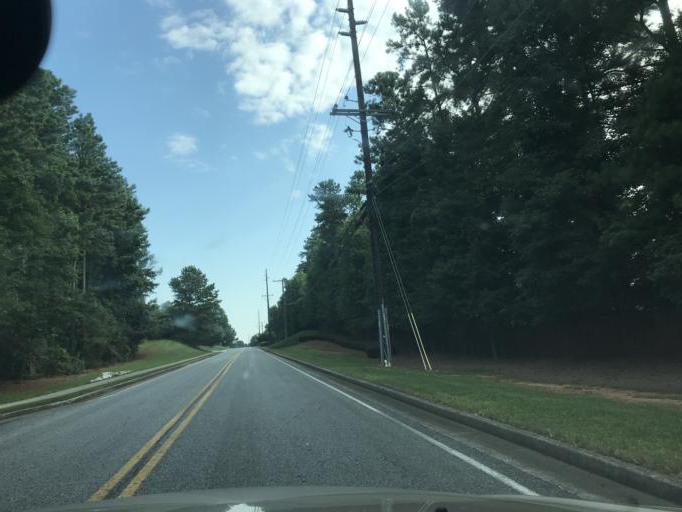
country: US
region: Georgia
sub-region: Fulton County
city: Johns Creek
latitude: 34.0629
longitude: -84.1532
